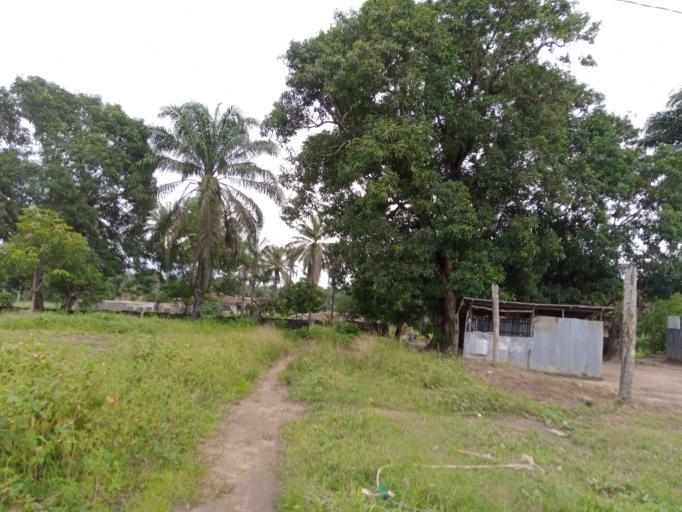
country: SL
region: Northern Province
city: Masoyila
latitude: 8.5985
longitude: -13.2025
